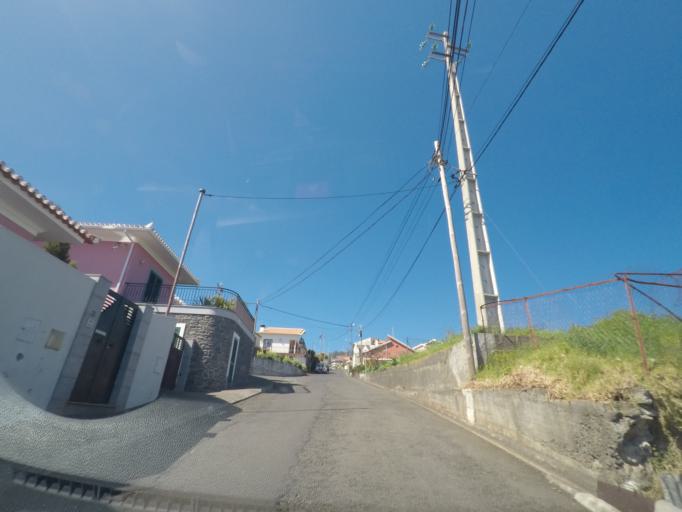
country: PT
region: Madeira
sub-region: Calheta
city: Arco da Calheta
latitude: 32.7030
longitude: -17.1165
